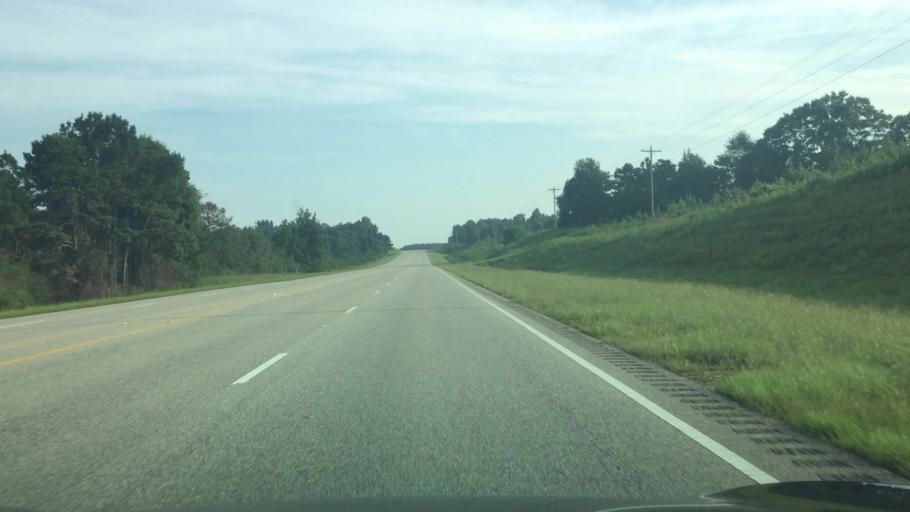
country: US
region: Alabama
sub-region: Covington County
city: Andalusia
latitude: 31.4281
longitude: -86.6116
